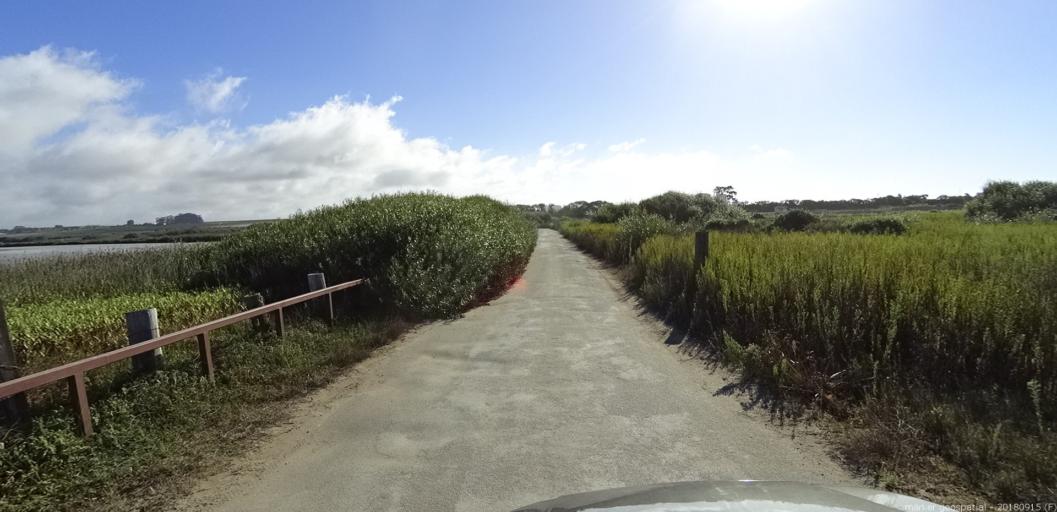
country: US
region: California
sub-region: Monterey County
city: Elkhorn
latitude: 36.8366
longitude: -121.8032
